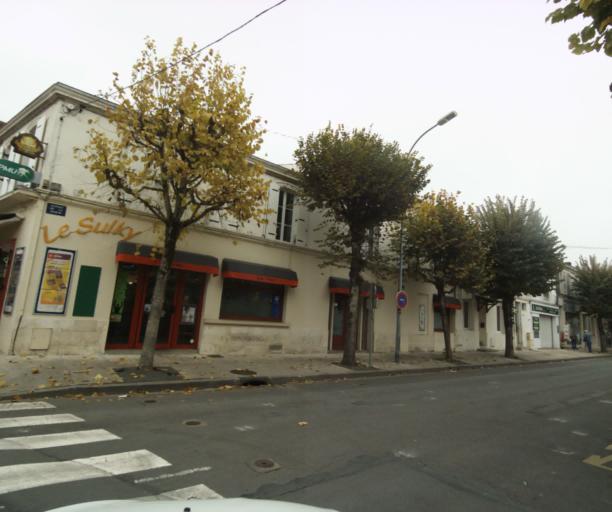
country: FR
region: Poitou-Charentes
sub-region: Departement de la Charente-Maritime
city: Saintes
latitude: 45.7463
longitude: -0.6185
